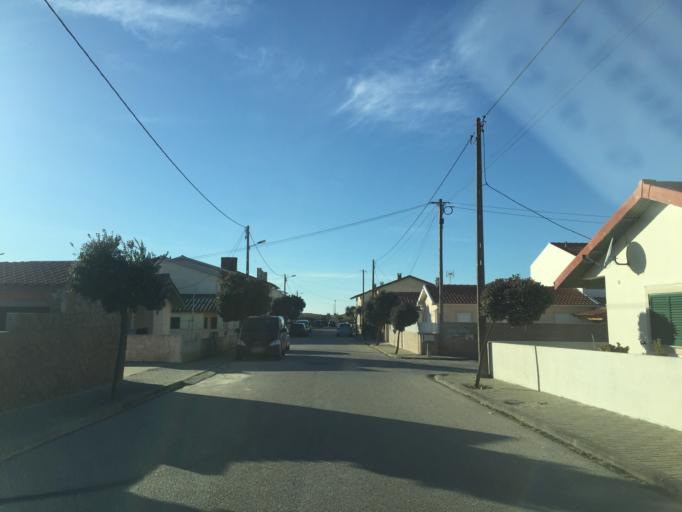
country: PT
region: Coimbra
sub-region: Figueira da Foz
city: Lavos
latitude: 40.0881
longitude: -8.8739
